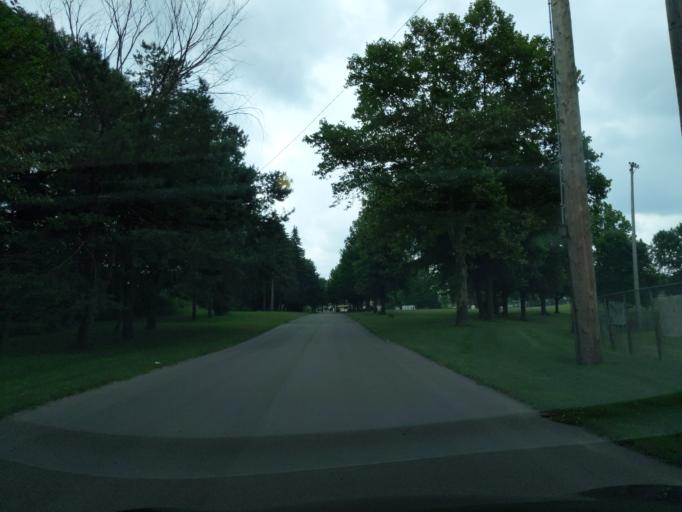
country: US
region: Michigan
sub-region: Ingham County
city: Lansing
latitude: 42.7620
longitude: -84.5461
